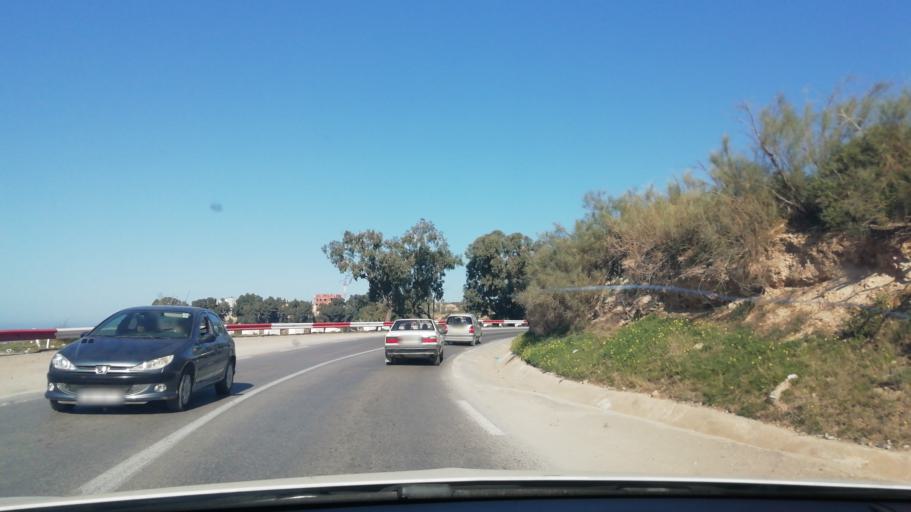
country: DZ
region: Tlemcen
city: Nedroma
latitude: 35.0917
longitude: -1.8712
